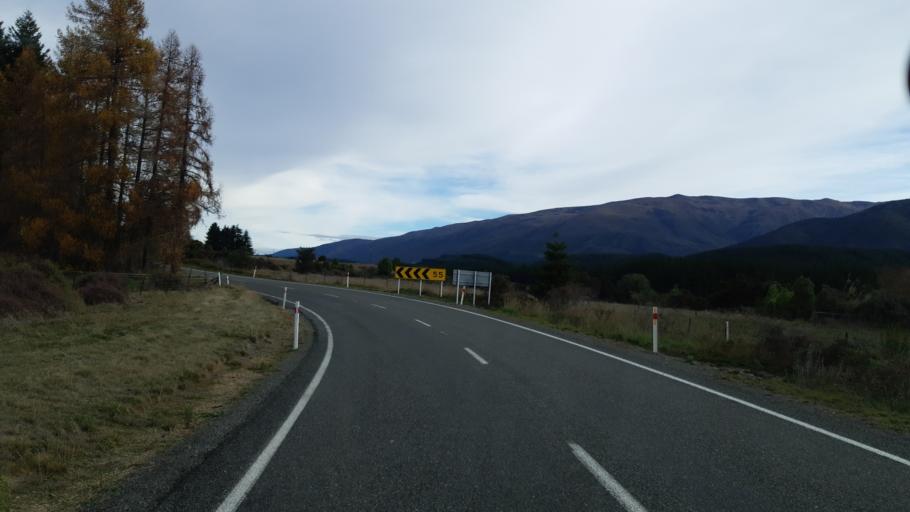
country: NZ
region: Tasman
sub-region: Tasman District
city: Brightwater
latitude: -41.6839
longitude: 173.1654
